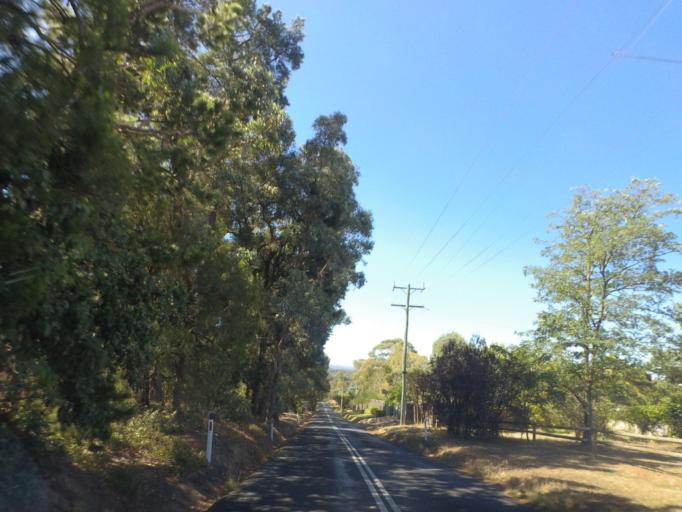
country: AU
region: Victoria
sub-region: Maroondah
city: Warranwood
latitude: -37.7600
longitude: 145.2531
